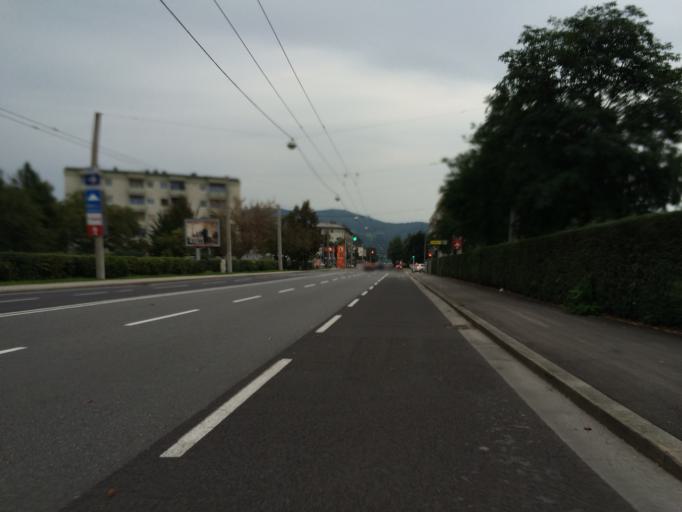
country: AT
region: Upper Austria
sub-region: Linz Stadt
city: Linz
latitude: 48.3000
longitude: 14.3060
